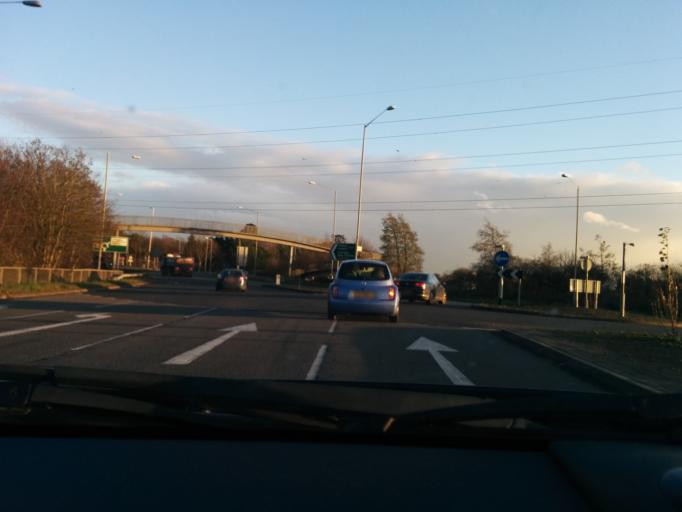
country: GB
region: England
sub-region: Buckinghamshire
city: Denham
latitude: 51.5602
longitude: -0.4962
